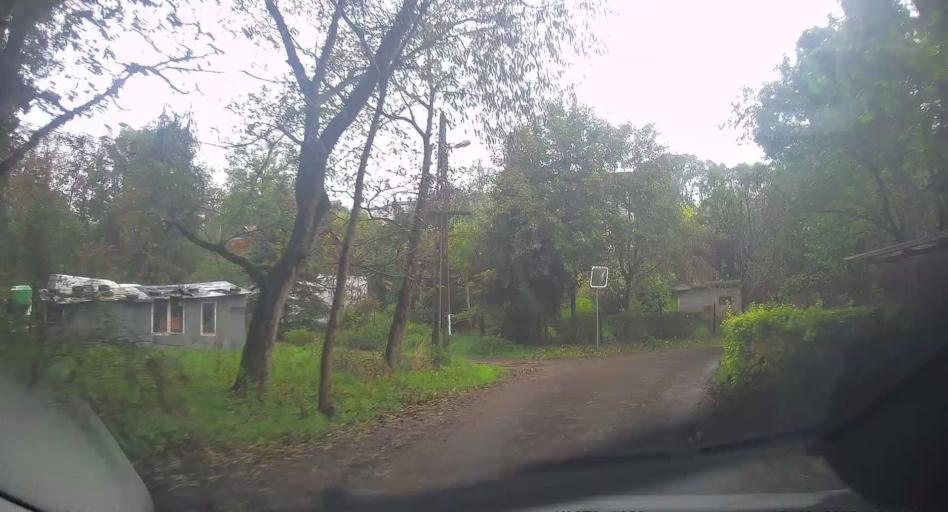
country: PL
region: Lesser Poland Voivodeship
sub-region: Powiat krakowski
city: Ochojno
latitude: 49.9931
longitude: 19.9900
